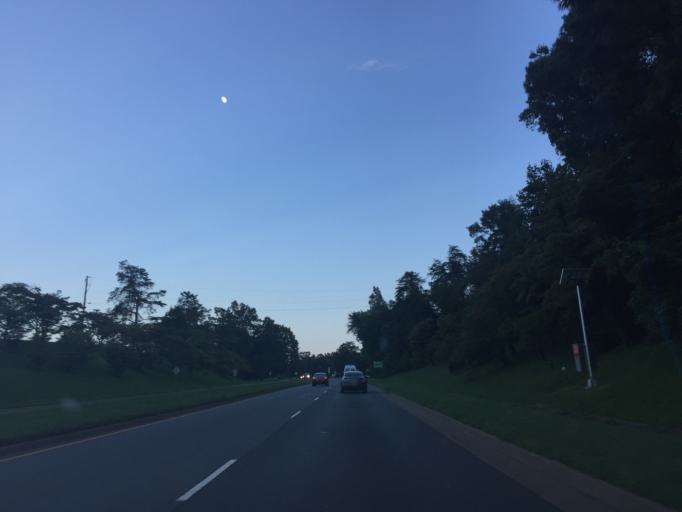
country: US
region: Virginia
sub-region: City of Charlottesville
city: Charlottesville
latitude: 38.0489
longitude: -78.4803
